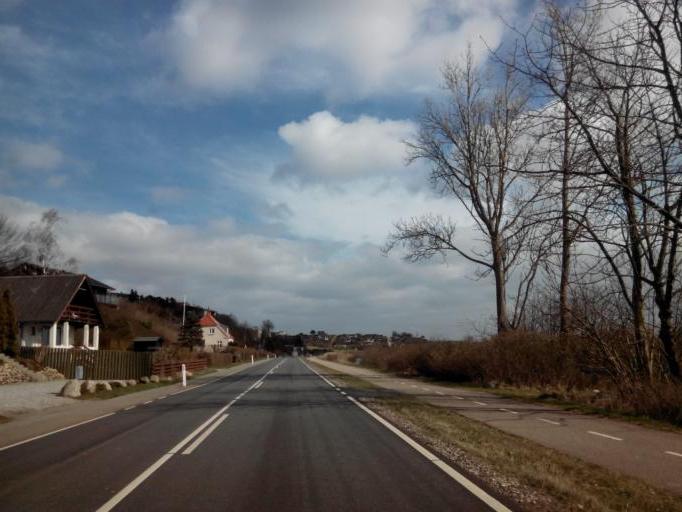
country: DK
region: Central Jutland
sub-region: Syddjurs Kommune
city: Ebeltoft
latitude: 56.2269
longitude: 10.6324
